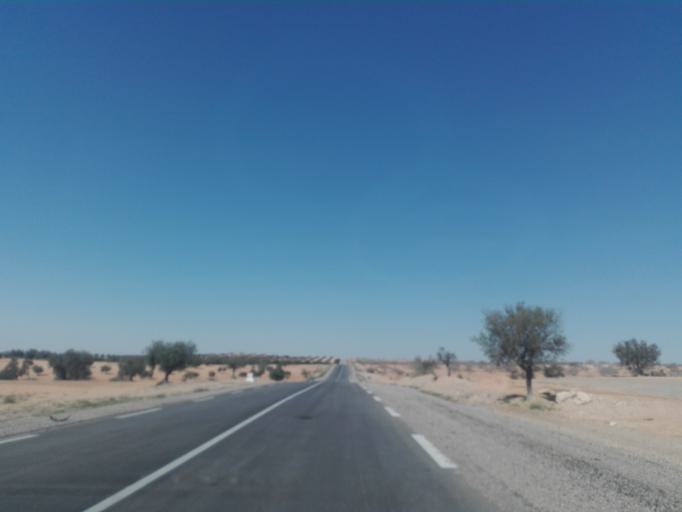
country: TN
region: Safaqis
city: Bi'r `Ali Bin Khalifah
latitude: 34.7584
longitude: 10.2929
